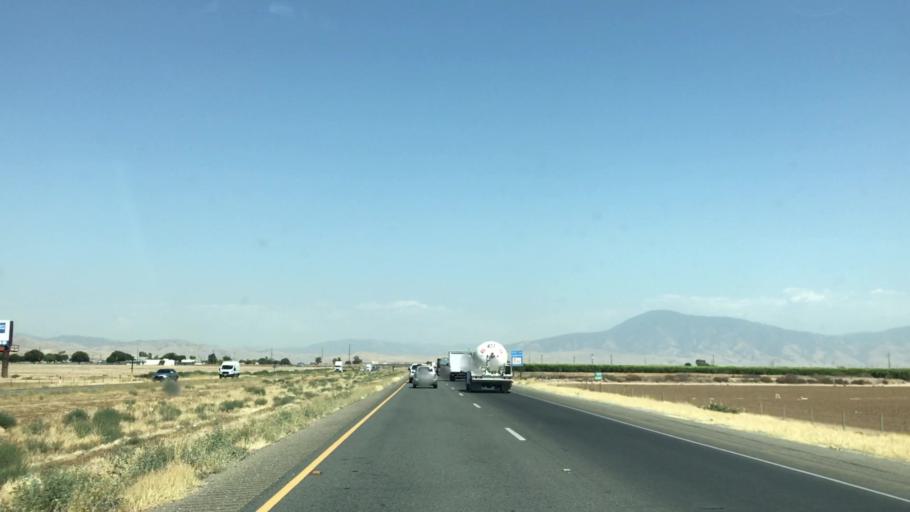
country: US
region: California
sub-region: Kern County
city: Lamont
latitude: 35.3484
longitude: -118.8893
